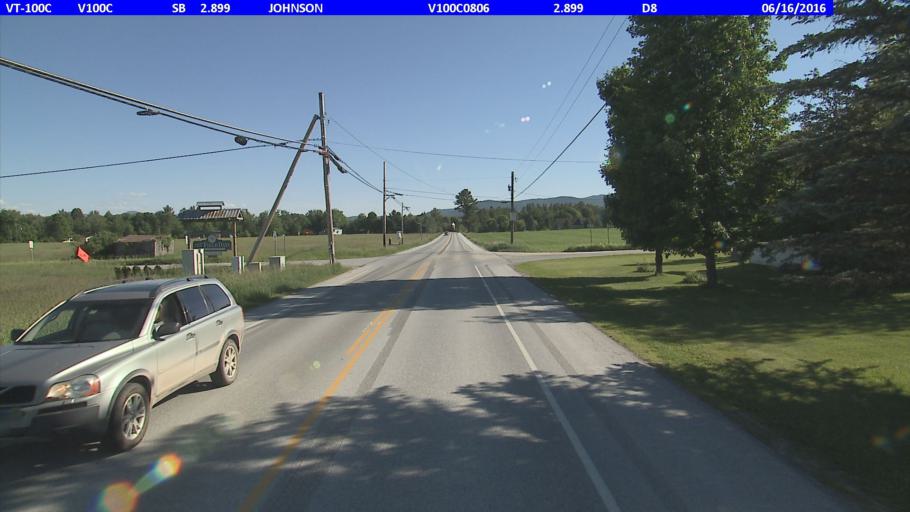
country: US
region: Vermont
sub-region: Lamoille County
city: Johnson
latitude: 44.6544
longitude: -72.6315
